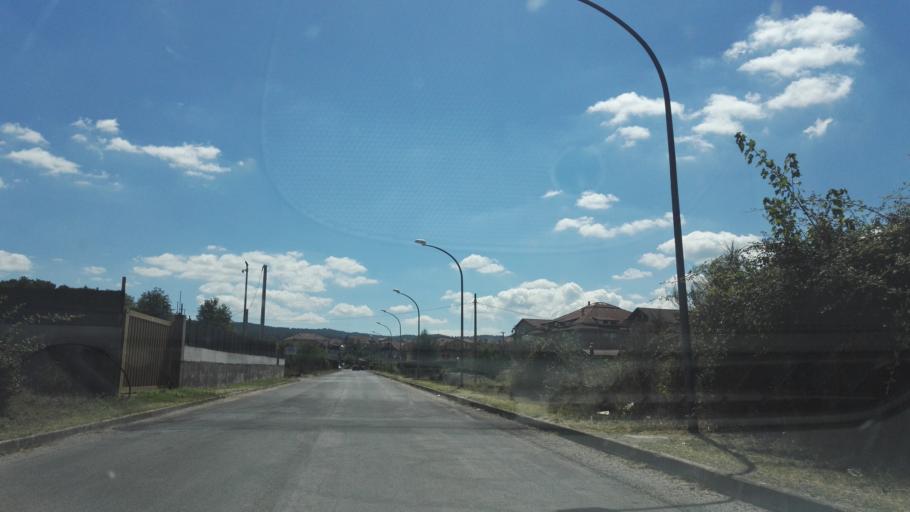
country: IT
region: Calabria
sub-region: Provincia di Vibo-Valentia
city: Serra San Bruno
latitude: 38.5709
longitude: 16.3292
